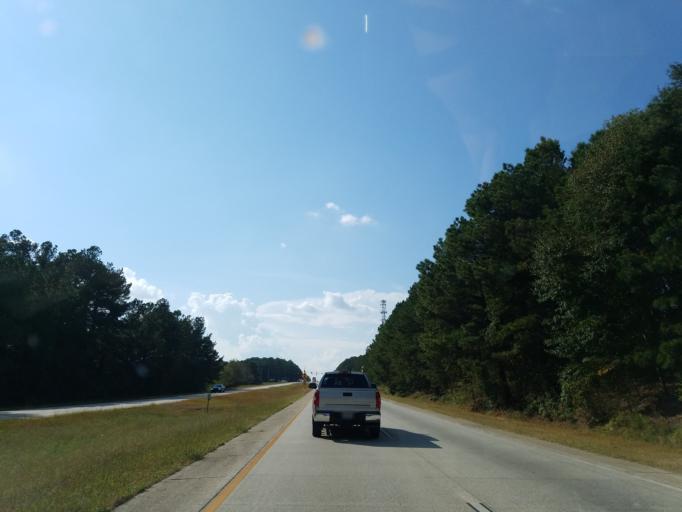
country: US
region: Georgia
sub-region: Barrow County
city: Auburn
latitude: 33.9607
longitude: -83.7922
